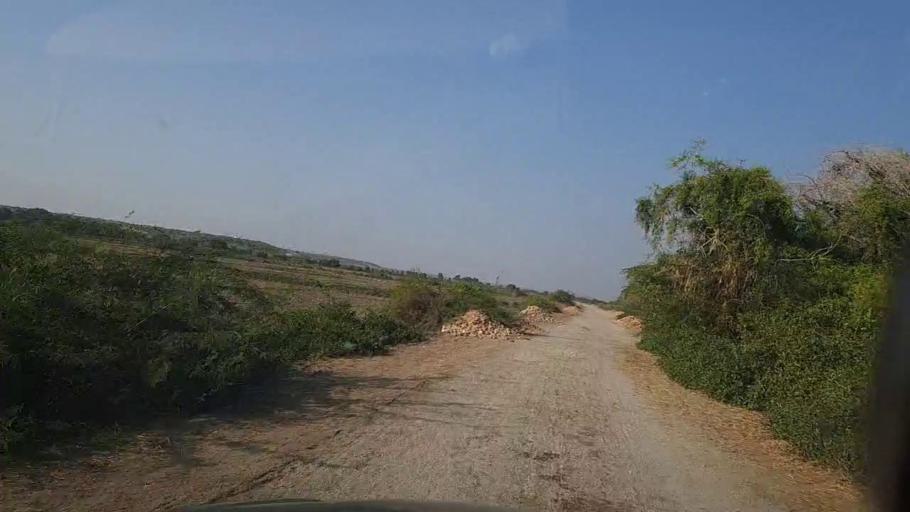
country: PK
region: Sindh
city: Thatta
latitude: 24.5880
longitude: 67.8766
